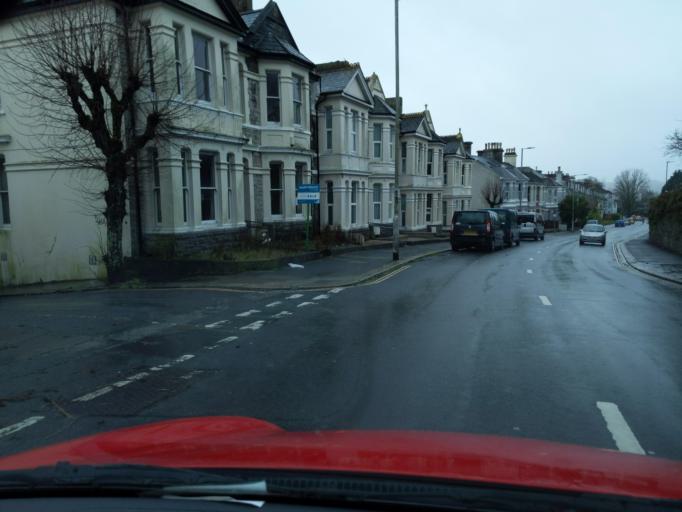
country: GB
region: England
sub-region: Plymouth
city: Plymouth
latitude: 50.3765
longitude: -4.1270
